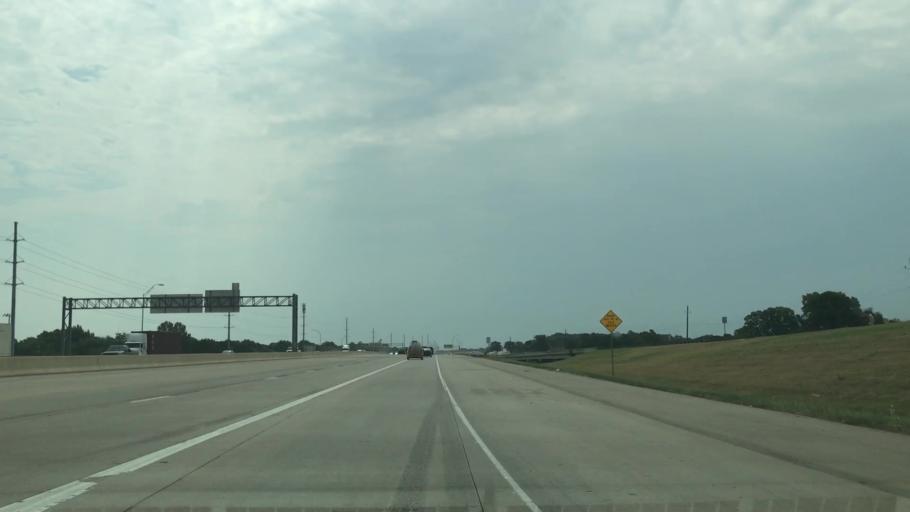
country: US
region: Texas
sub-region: Denton County
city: Roanoke
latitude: 32.9972
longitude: -97.2074
